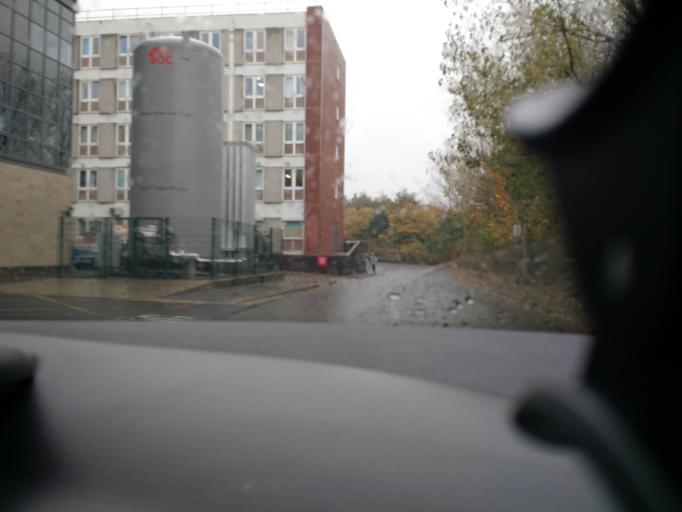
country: GB
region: England
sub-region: Lancashire
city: Great Marton
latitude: 53.8195
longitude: -3.0110
